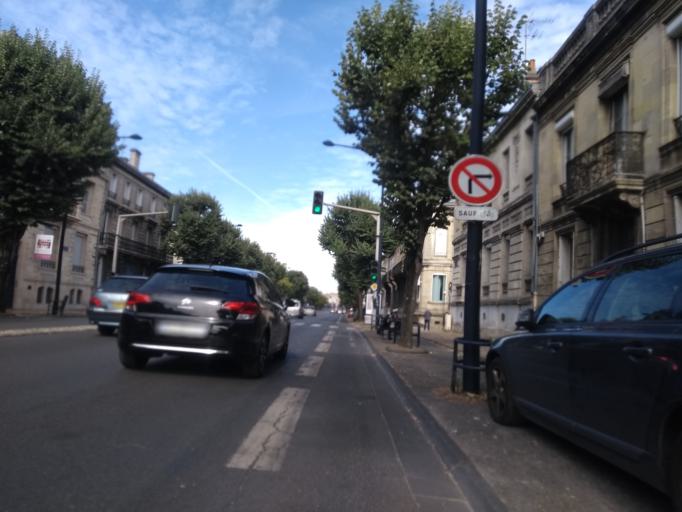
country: FR
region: Aquitaine
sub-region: Departement de la Gironde
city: Bordeaux
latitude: 44.8443
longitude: -0.5991
